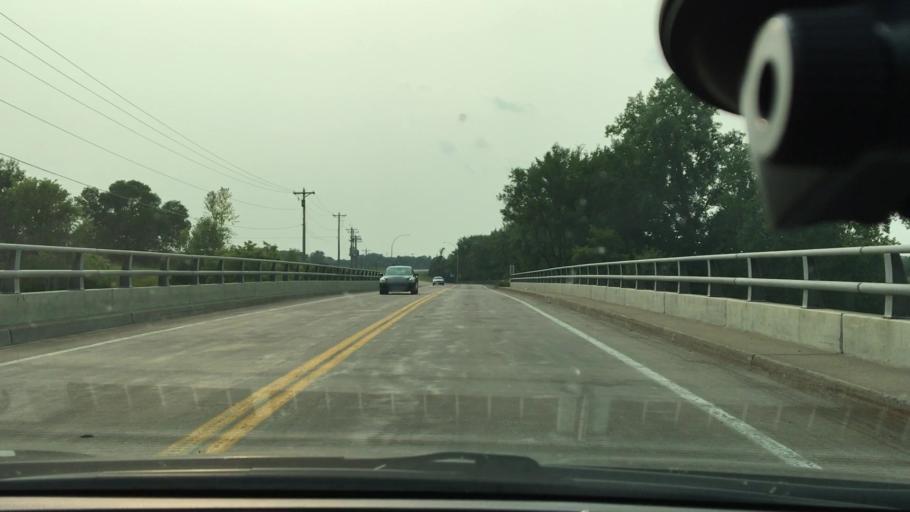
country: US
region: Minnesota
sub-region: Hennepin County
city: Dayton
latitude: 45.2444
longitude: -93.5219
